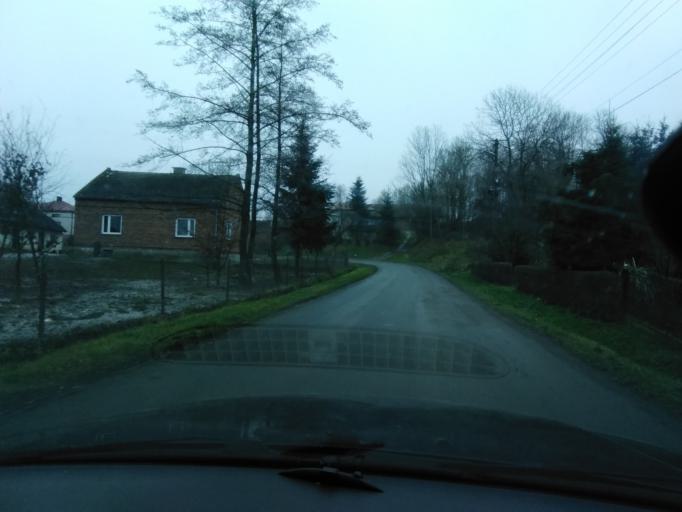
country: PL
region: Subcarpathian Voivodeship
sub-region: Powiat przeworski
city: Zarzecze
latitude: 49.9689
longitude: 22.5674
